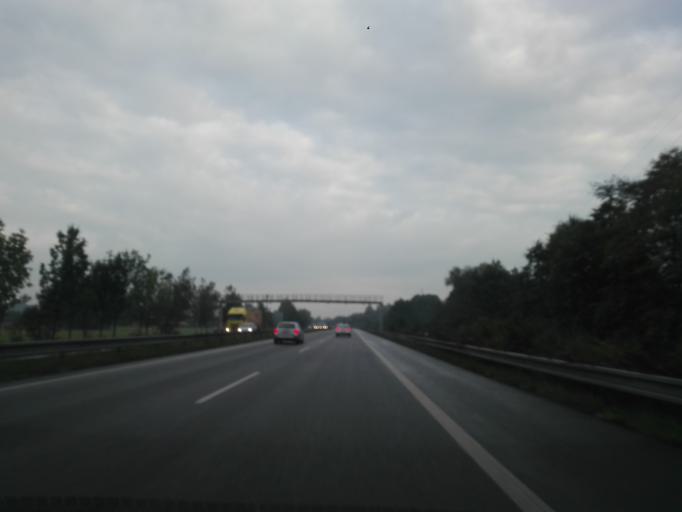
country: CZ
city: Paskov
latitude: 49.7456
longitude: 18.2796
